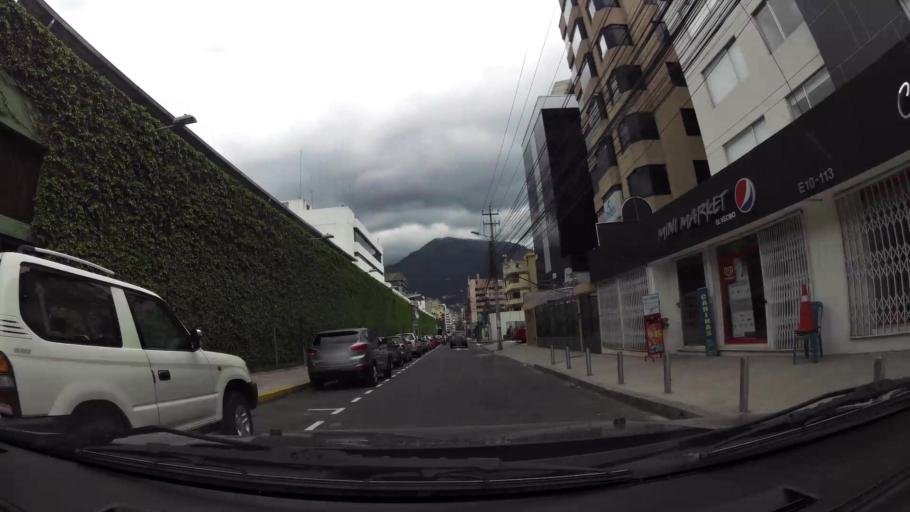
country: EC
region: Pichincha
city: Quito
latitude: -0.1760
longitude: -78.4785
